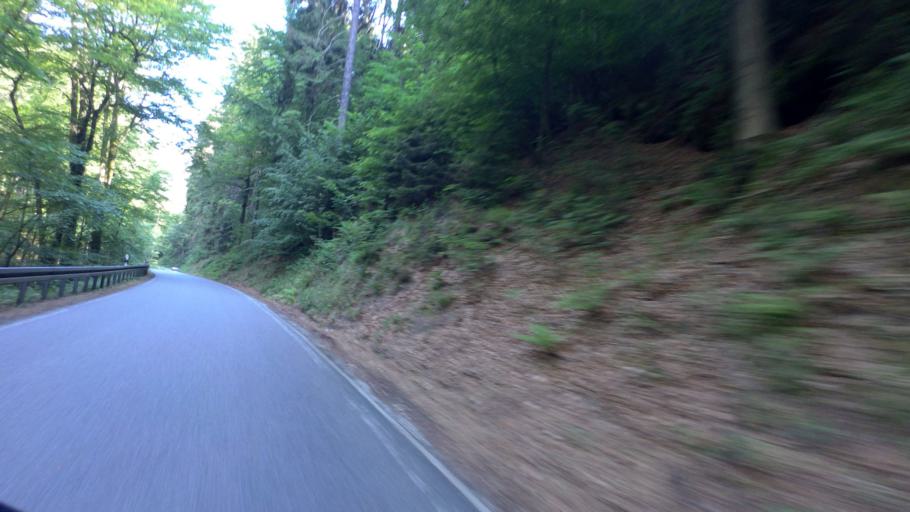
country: DE
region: Saxony
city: Porschdorf
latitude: 50.9504
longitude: 14.1352
